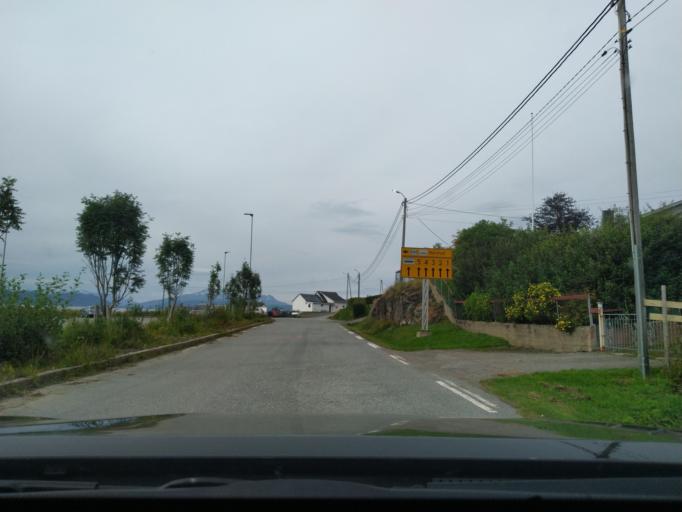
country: NO
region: Nordland
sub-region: Evenes
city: Randa
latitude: 68.7268
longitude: 16.8498
